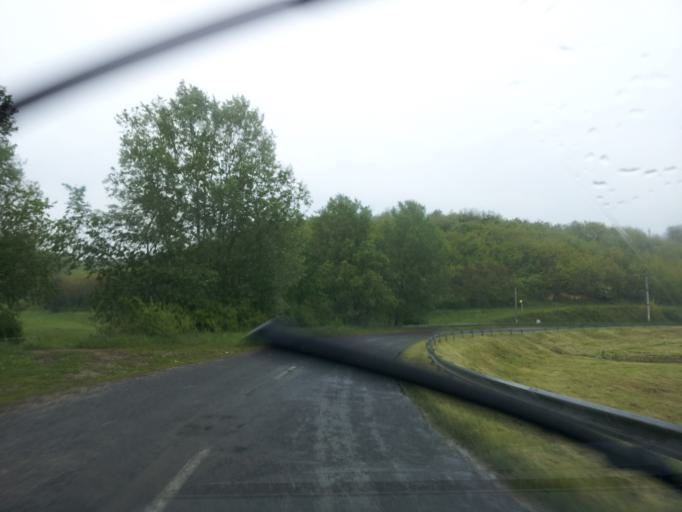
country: HU
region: Tolna
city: Szentgalpuszta
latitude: 46.2729
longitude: 18.6295
